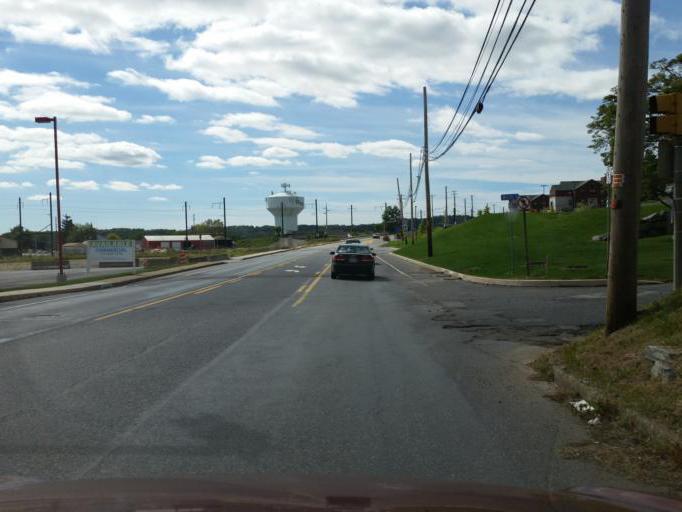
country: US
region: Pennsylvania
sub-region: Dauphin County
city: Middletown
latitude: 40.1980
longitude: -76.7358
